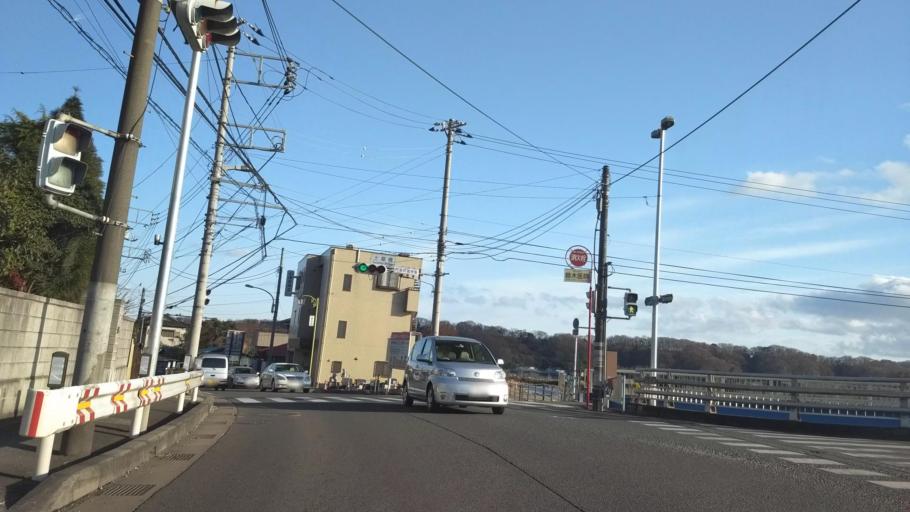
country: JP
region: Kanagawa
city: Hadano
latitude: 35.3563
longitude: 139.2699
